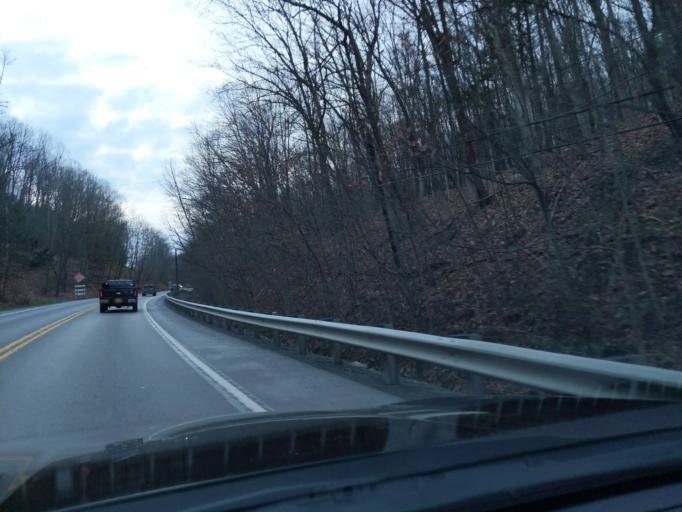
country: US
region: Pennsylvania
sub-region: Blair County
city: Williamsburg
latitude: 40.4696
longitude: -78.2916
